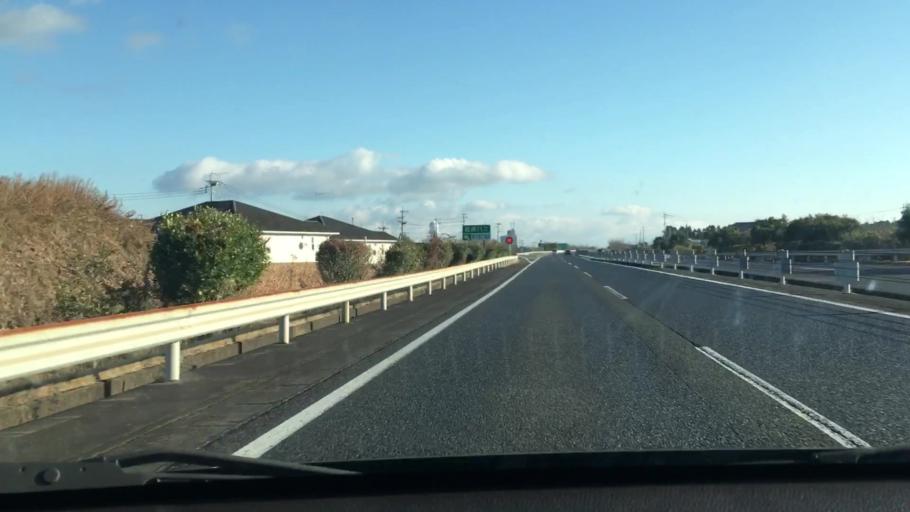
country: JP
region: Kagoshima
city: Kajiki
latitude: 31.8026
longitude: 130.7112
